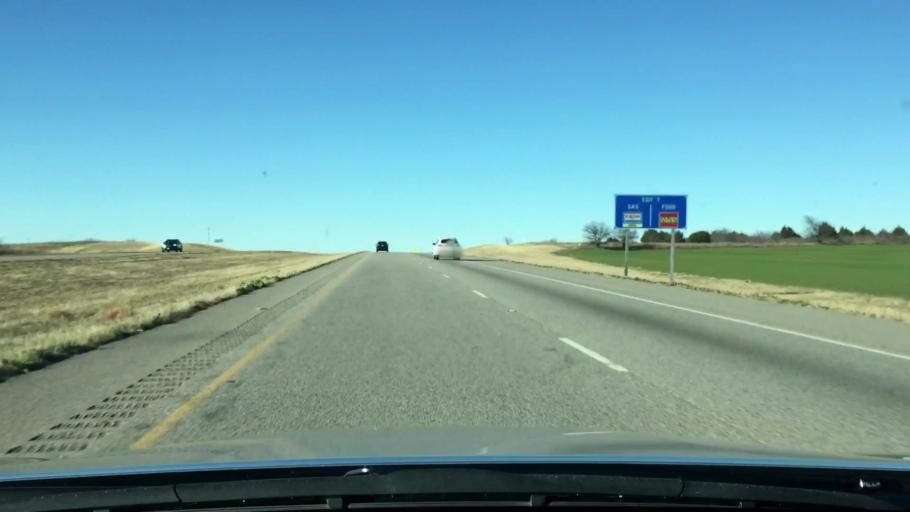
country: US
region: Texas
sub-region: Hill County
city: Itasca
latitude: 32.1397
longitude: -97.1220
